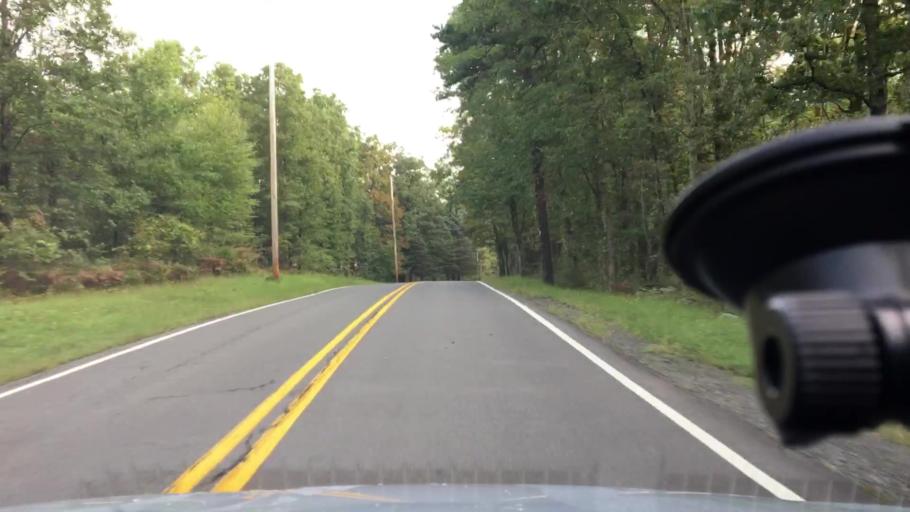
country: US
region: Pennsylvania
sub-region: Monroe County
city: Mountainhome
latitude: 41.1399
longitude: -75.2601
